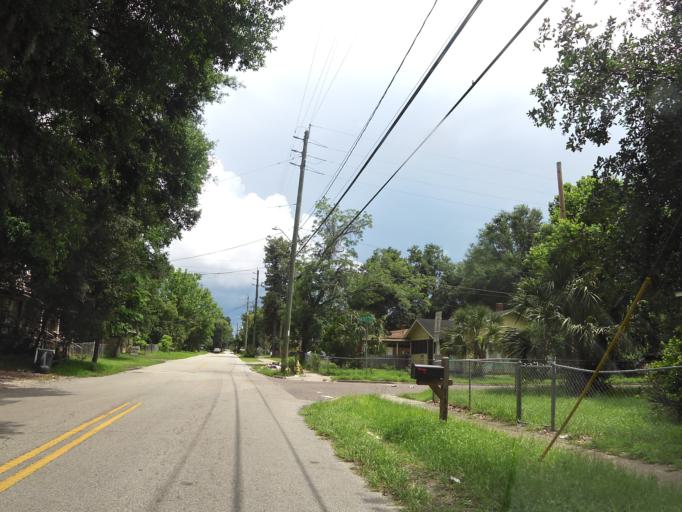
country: US
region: Florida
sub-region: Duval County
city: Jacksonville
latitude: 30.3848
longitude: -81.6410
